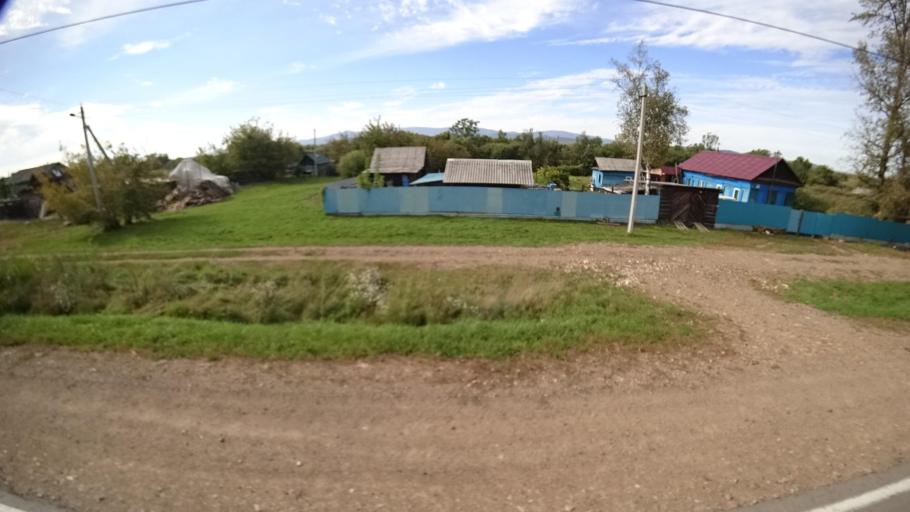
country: RU
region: Primorskiy
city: Dostoyevka
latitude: 44.3093
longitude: 133.4542
